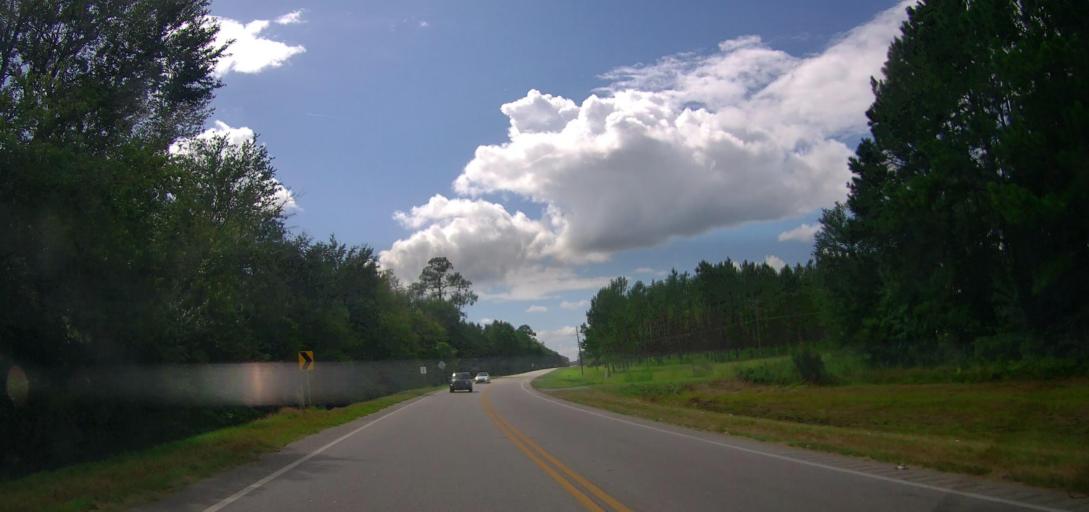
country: US
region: Georgia
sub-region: Coffee County
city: Broxton
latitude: 31.5474
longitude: -82.9446
